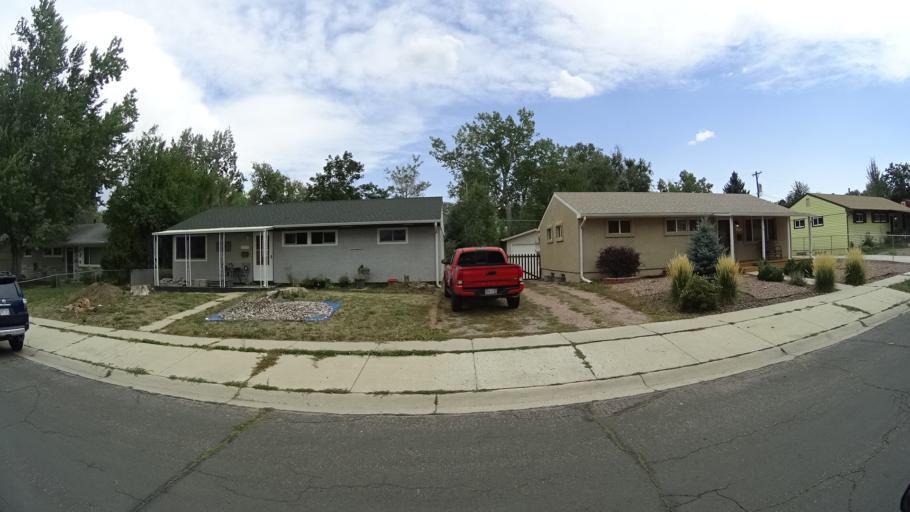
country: US
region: Colorado
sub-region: El Paso County
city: Colorado Springs
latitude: 38.8687
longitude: -104.7889
